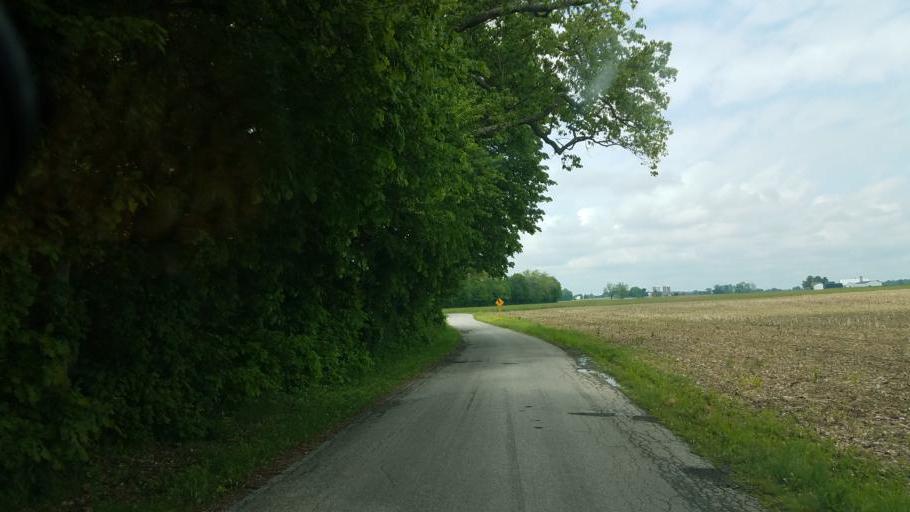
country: US
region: Ohio
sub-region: Marion County
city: Prospect
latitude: 40.3736
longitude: -83.1859
